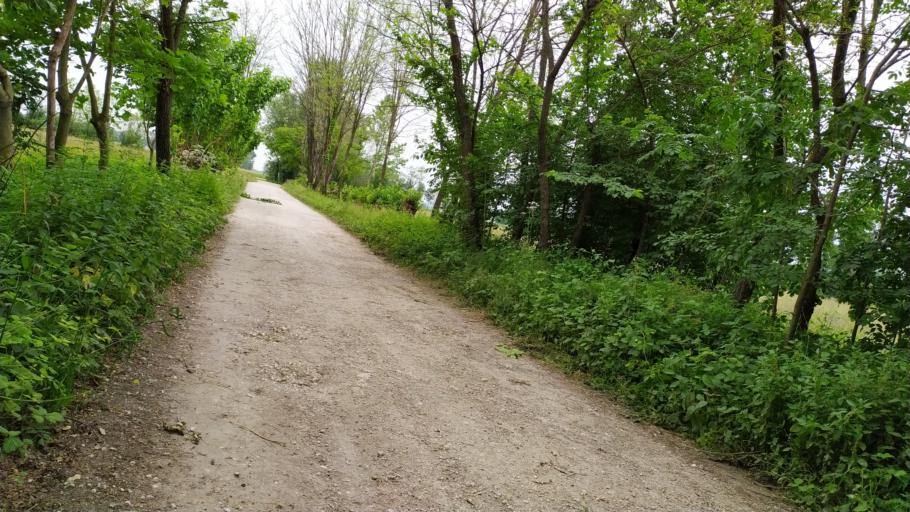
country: IT
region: Friuli Venezia Giulia
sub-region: Provincia di Udine
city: Osoppo
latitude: 46.2427
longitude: 13.0687
